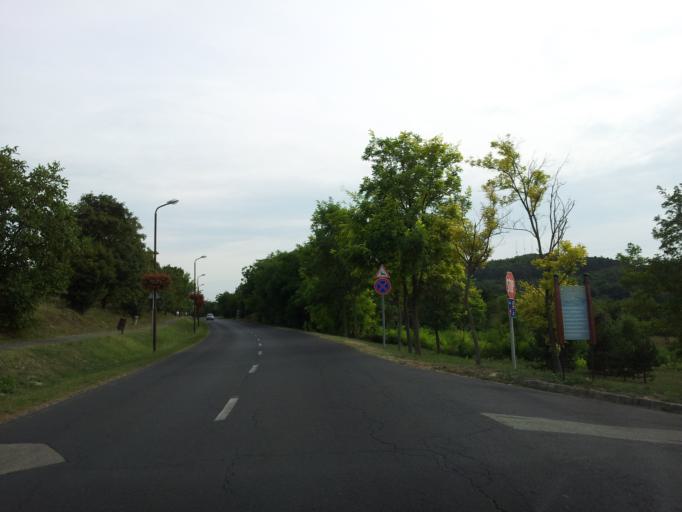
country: HU
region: Veszprem
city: Tihany
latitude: 46.9055
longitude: 17.8905
